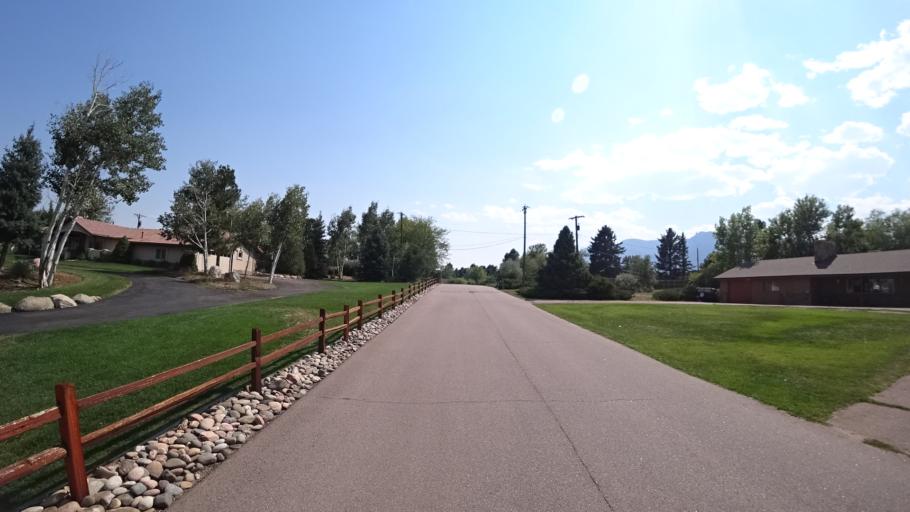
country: US
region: Colorado
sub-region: El Paso County
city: Colorado Springs
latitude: 38.7999
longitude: -104.8281
